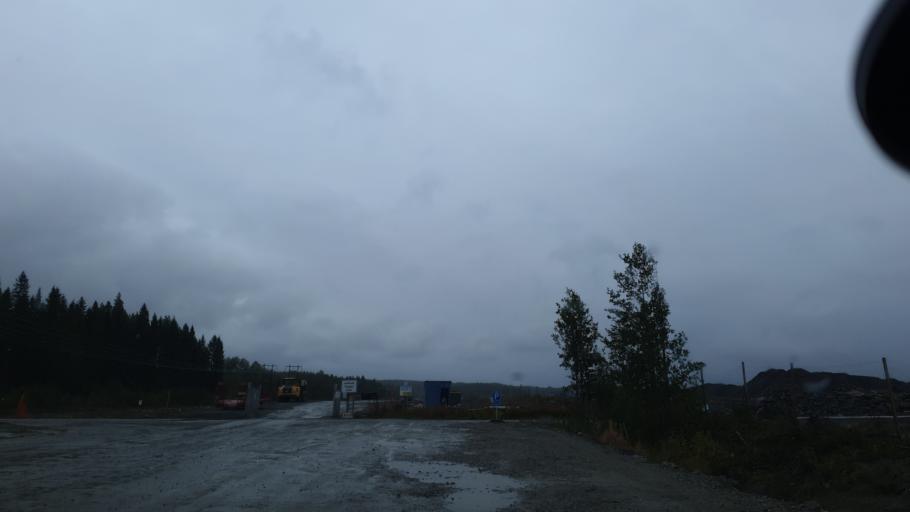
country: SE
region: Vaesterbotten
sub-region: Skelleftea Kommun
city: Soedra Bergsbyn
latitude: 64.7407
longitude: 21.0762
